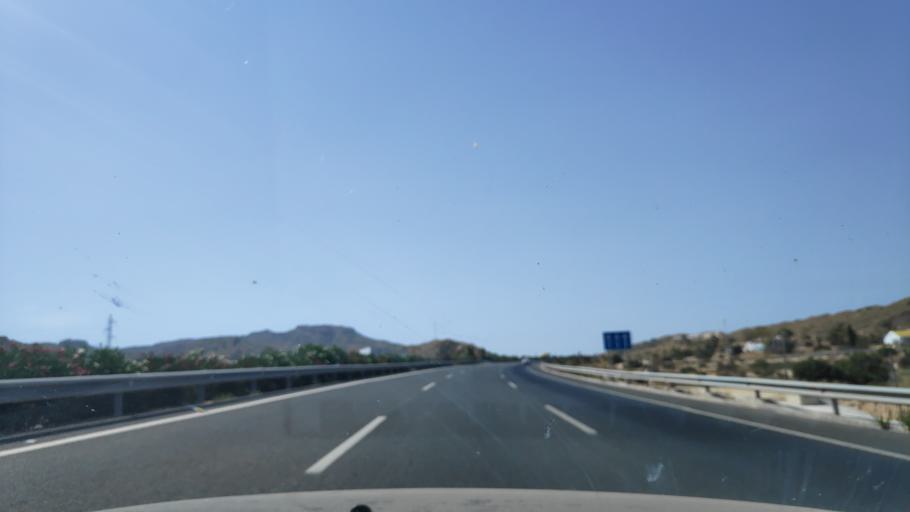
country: ES
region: Murcia
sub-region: Murcia
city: Ulea
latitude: 38.1563
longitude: -1.2966
